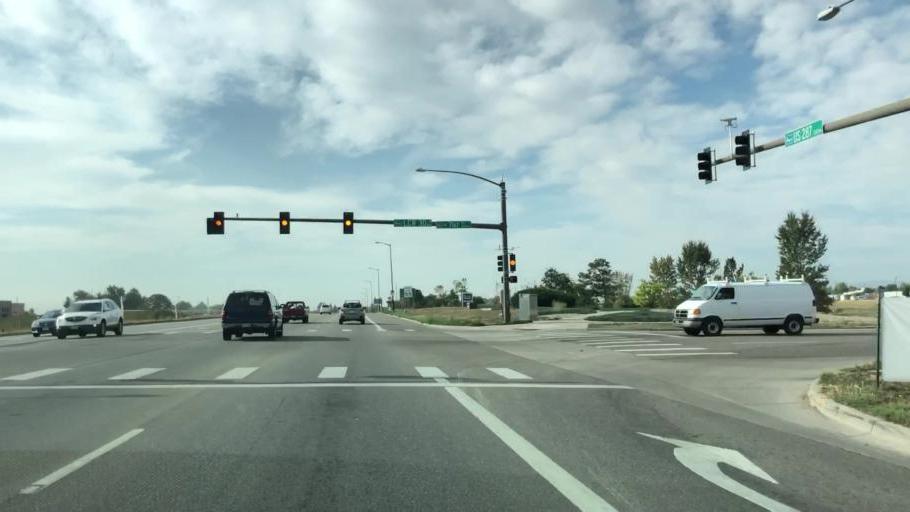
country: US
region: Colorado
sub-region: Larimer County
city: Loveland
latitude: 40.4658
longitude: -105.0775
